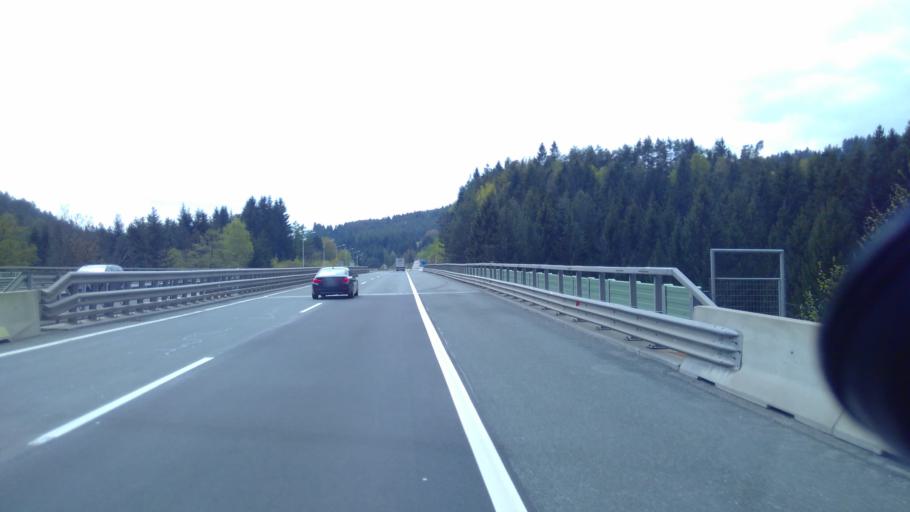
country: AT
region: Styria
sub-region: Politischer Bezirk Deutschlandsberg
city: Gundersdorf
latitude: 46.9611
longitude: 15.2188
